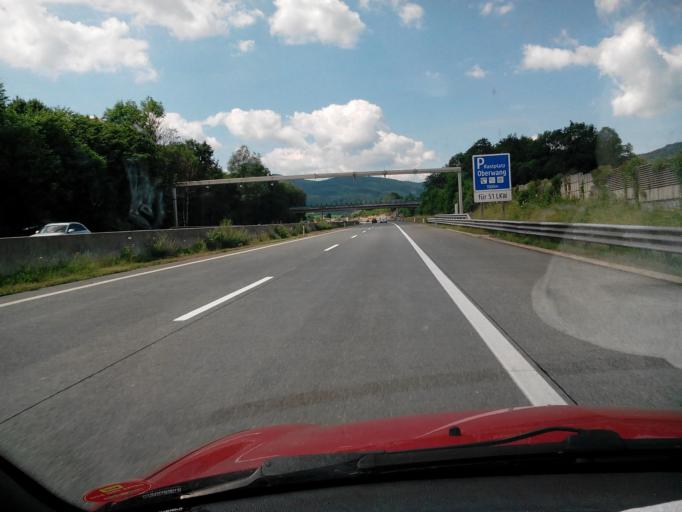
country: AT
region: Upper Austria
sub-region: Politischer Bezirk Vocklabruck
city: Oberwang
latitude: 47.8944
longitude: 13.4398
